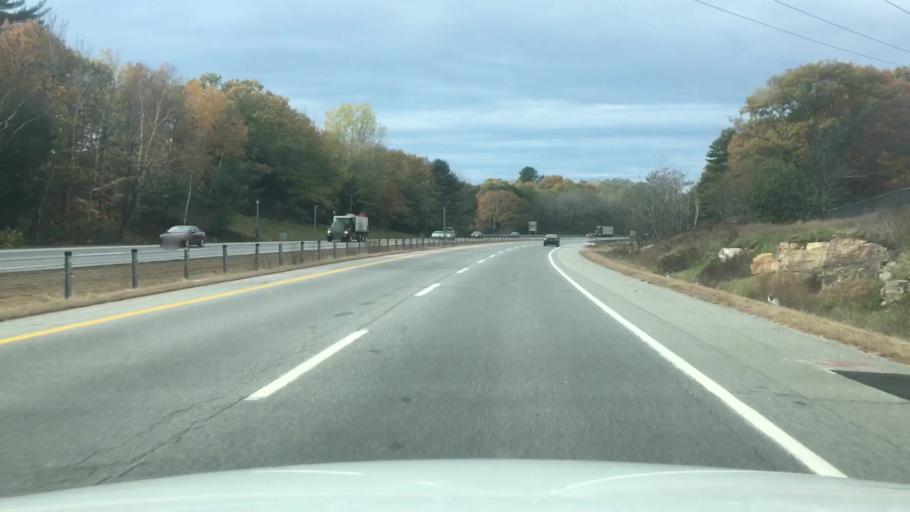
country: US
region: Maine
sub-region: Cumberland County
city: Brunswick
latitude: 43.9093
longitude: -69.9239
